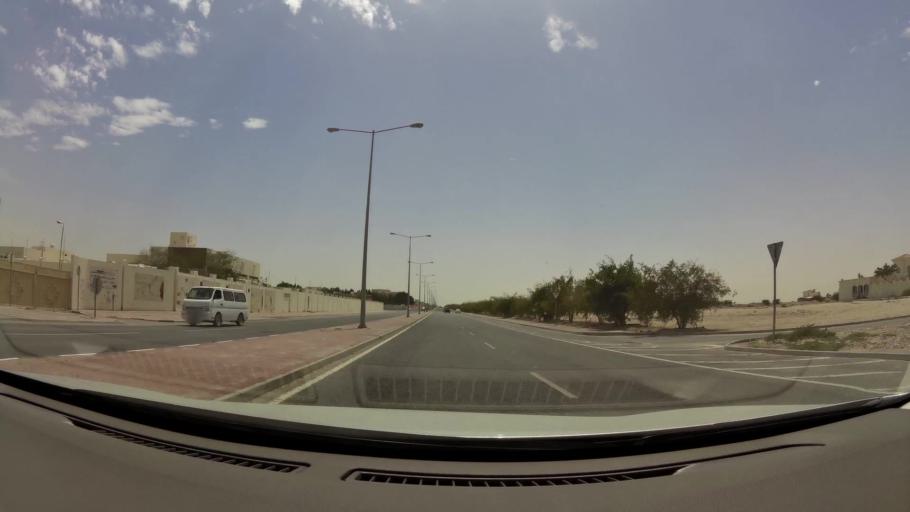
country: QA
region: Baladiyat ar Rayyan
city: Ar Rayyan
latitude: 25.2952
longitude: 51.4066
